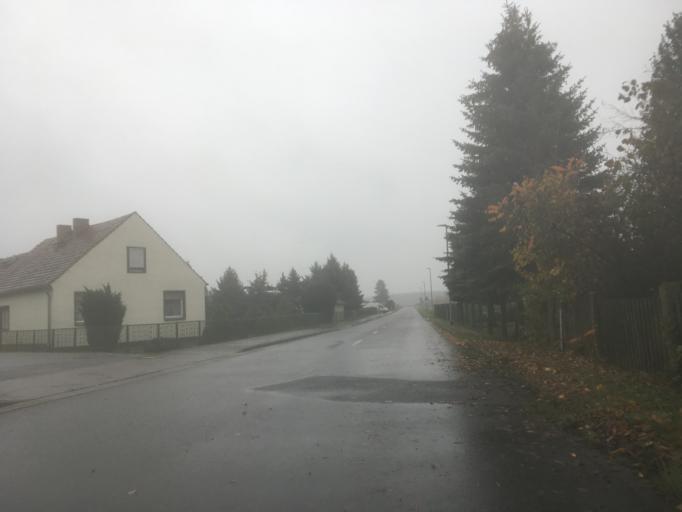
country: DE
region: Brandenburg
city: Schlepzig
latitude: 52.0268
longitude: 13.9845
